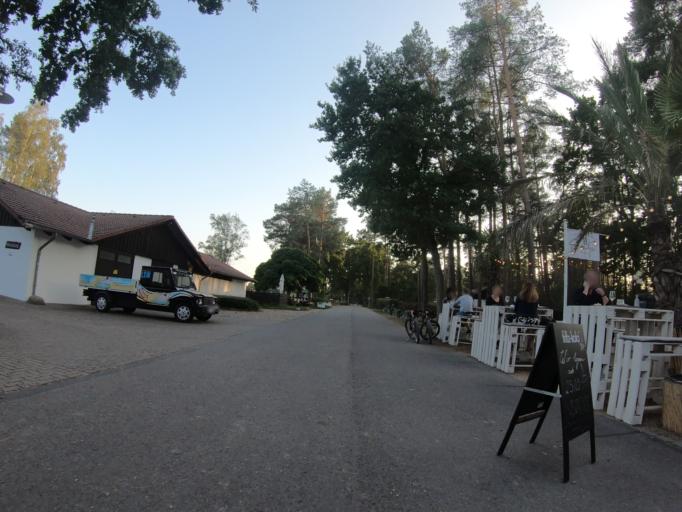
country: DE
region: Lower Saxony
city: Calberlah
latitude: 52.4565
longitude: 10.6185
